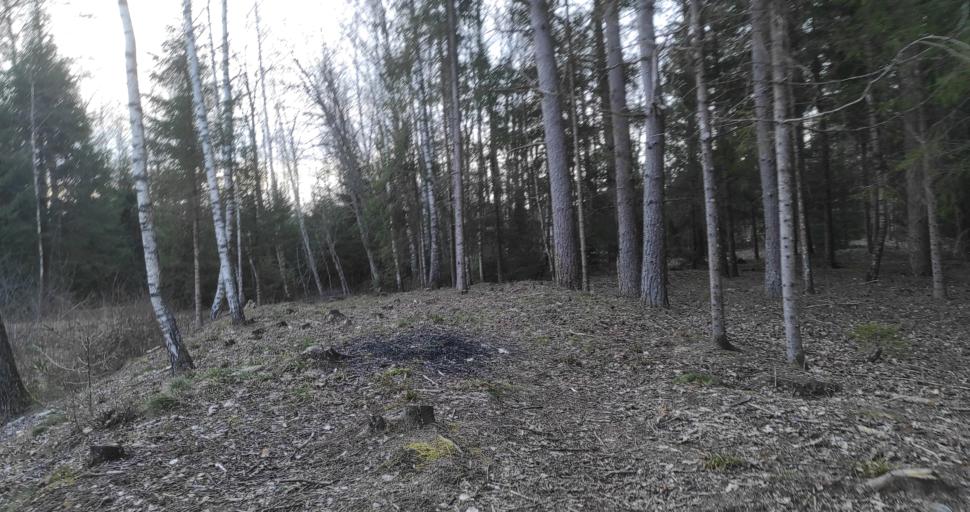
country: LV
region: Kuldigas Rajons
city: Kuldiga
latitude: 56.9105
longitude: 21.8909
